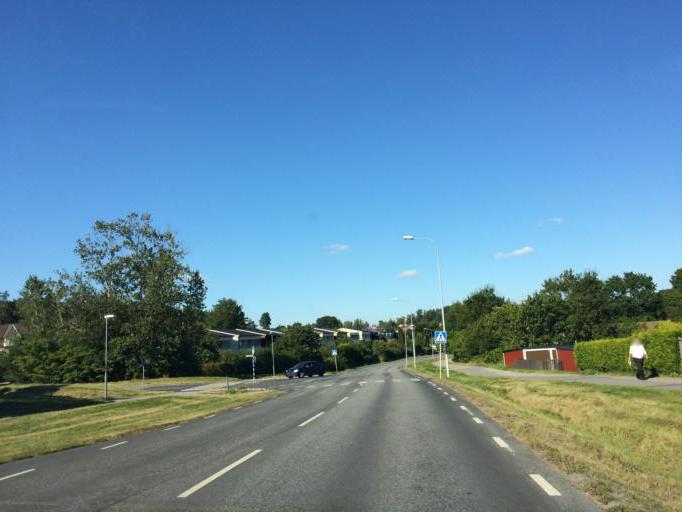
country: SE
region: Stockholm
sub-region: Upplands Vasby Kommun
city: Upplands Vaesby
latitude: 59.4936
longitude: 17.9486
